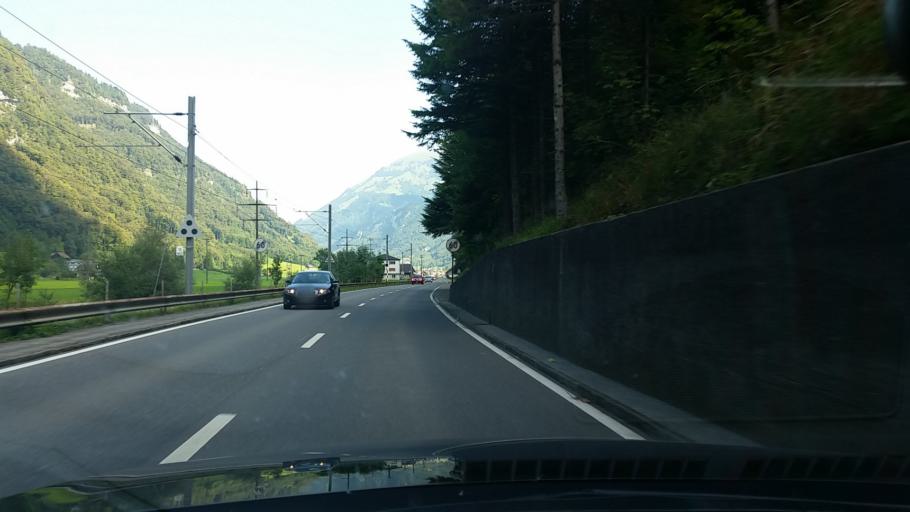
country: CH
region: Nidwalden
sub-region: Nidwalden
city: Wolfenschiessen
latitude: 46.8820
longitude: 8.3783
